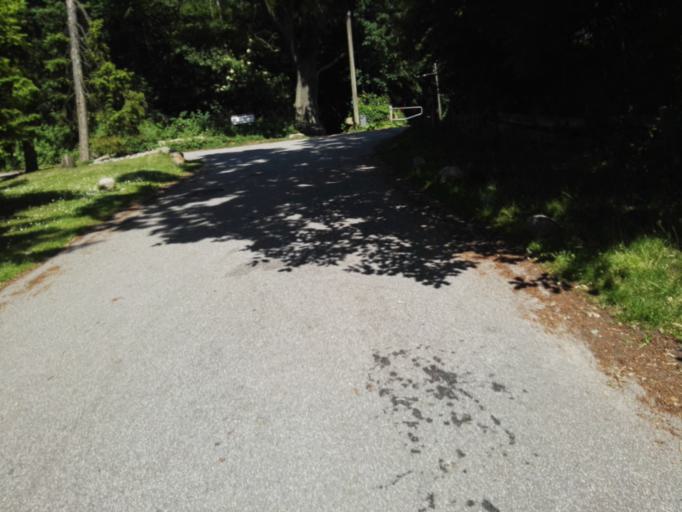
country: DK
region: Capital Region
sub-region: Ballerup Kommune
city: Ballerup
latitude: 55.7530
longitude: 12.3842
